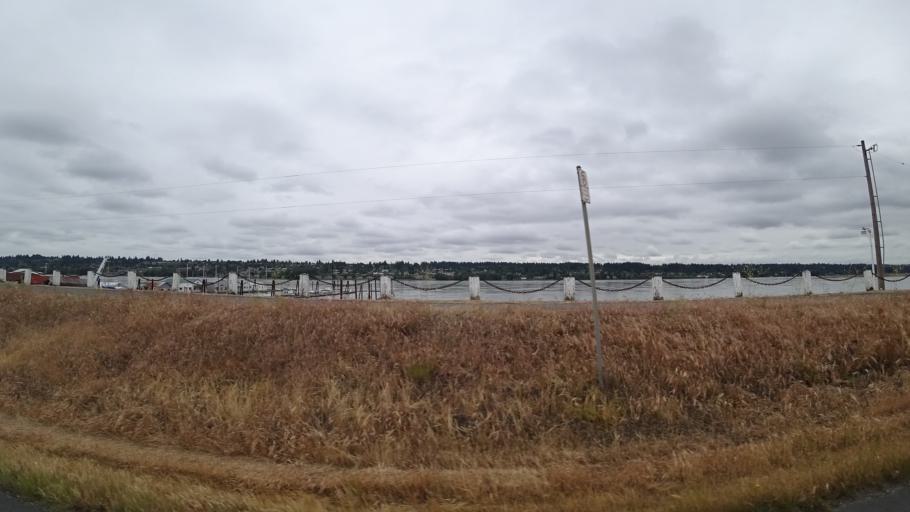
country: US
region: Washington
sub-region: Clark County
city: Walnut Grove
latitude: 45.5949
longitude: -122.5897
